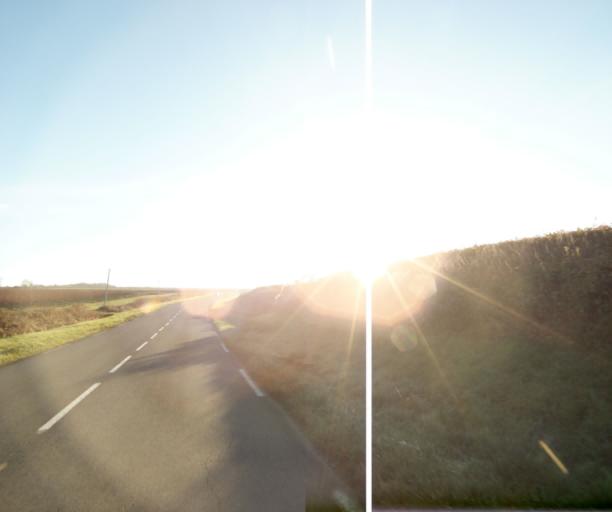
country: FR
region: Poitou-Charentes
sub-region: Departement de la Charente-Maritime
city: Cherac
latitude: 45.6969
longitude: -0.4334
